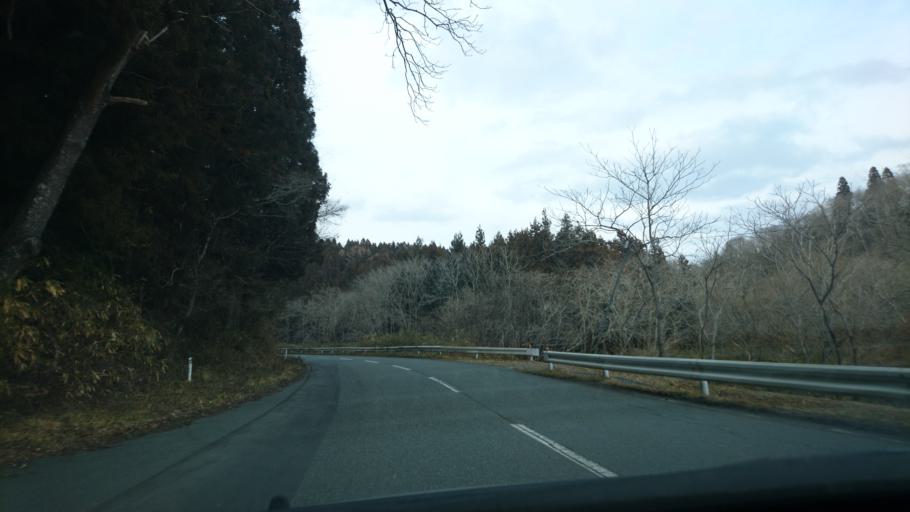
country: JP
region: Iwate
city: Ichinoseki
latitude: 38.8549
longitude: 141.3031
